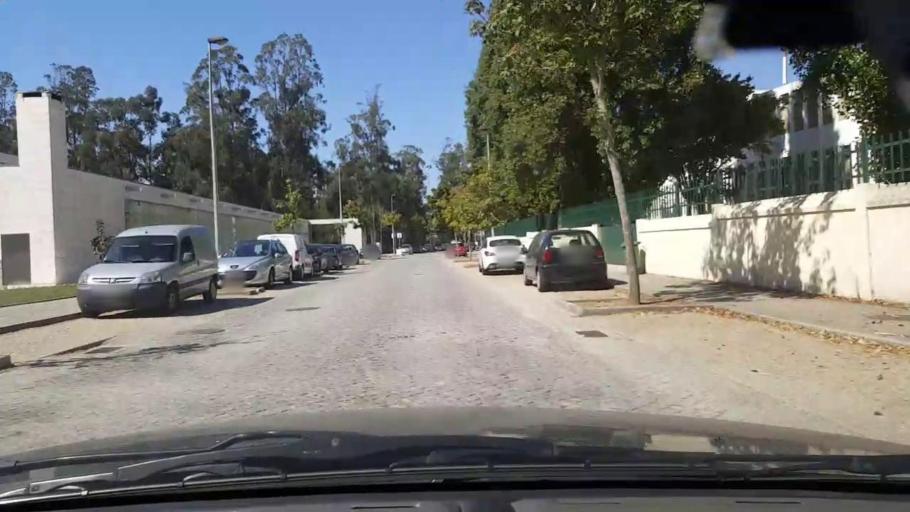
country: PT
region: Porto
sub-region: Vila do Conde
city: Arvore
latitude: 41.3086
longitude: -8.7201
